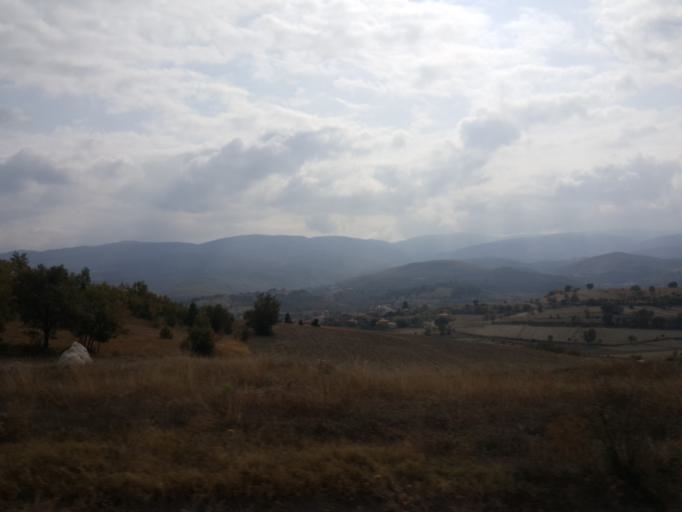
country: TR
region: Sinop
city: Sarayduzu
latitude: 41.3425
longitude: 34.8042
